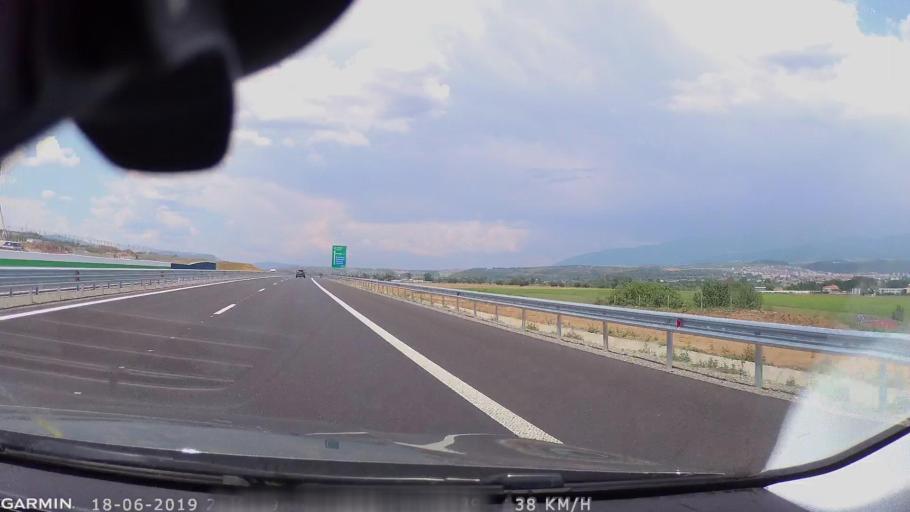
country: BG
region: Blagoevgrad
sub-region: Obshtina Blagoevgrad
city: Blagoevgrad
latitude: 41.9794
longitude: 23.0654
